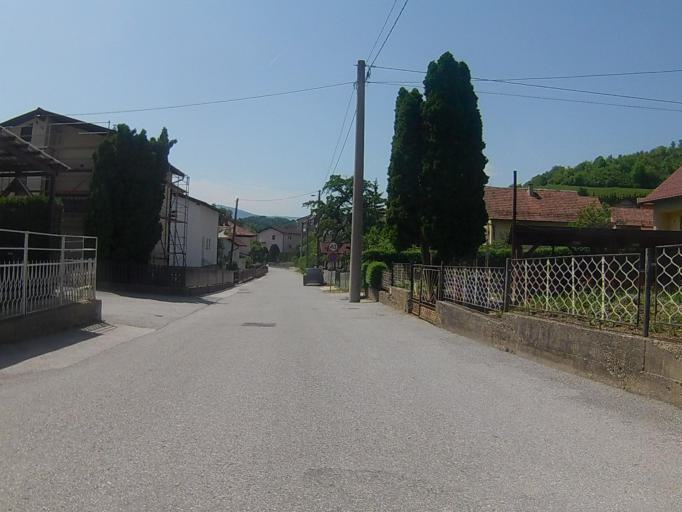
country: SI
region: Pesnica
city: Pesnica pri Mariboru
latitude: 46.5773
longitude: 15.6685
